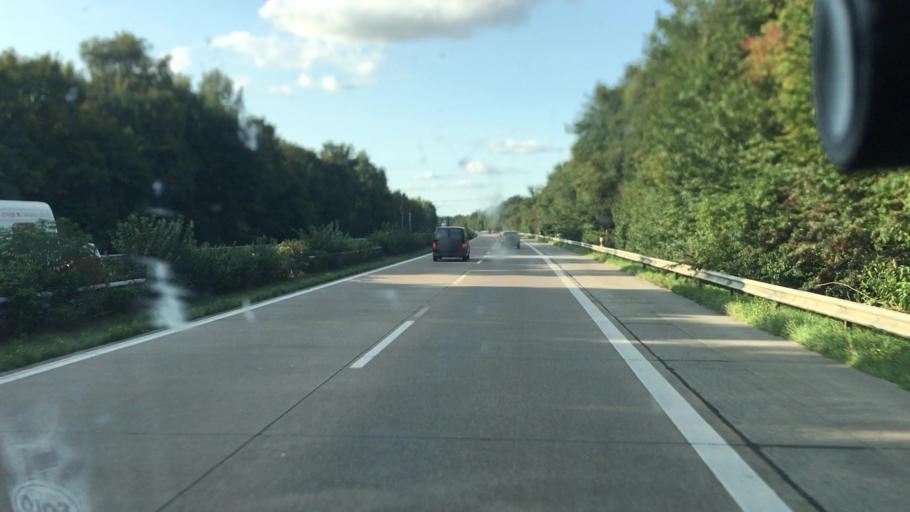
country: DE
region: Lower Saxony
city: Rastede
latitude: 53.2504
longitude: 8.1743
